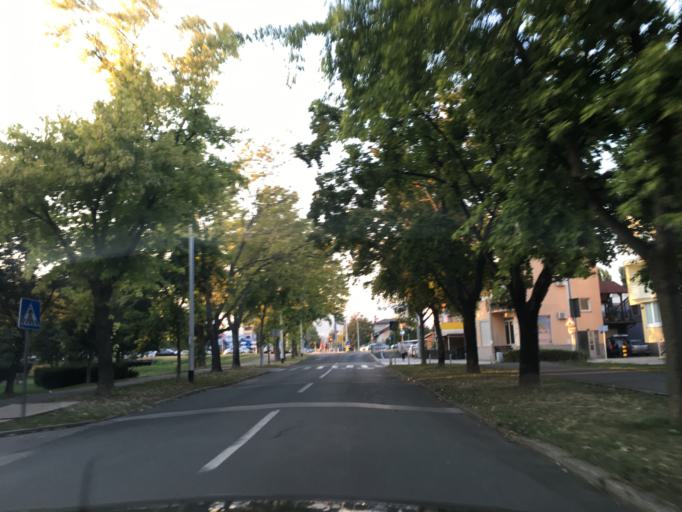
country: HR
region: Grad Zagreb
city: Jankomir
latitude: 45.7929
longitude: 15.9409
